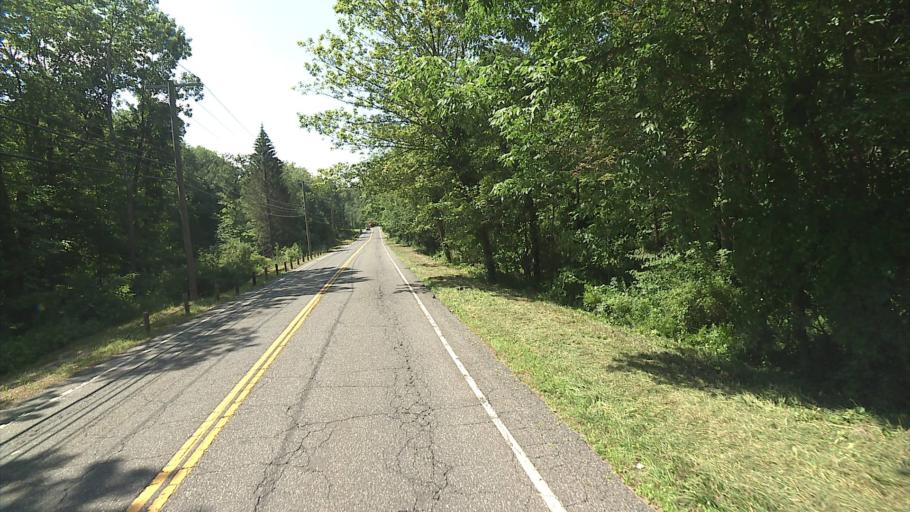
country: US
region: Connecticut
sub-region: Litchfield County
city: New Preston
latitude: 41.7120
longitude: -73.3453
